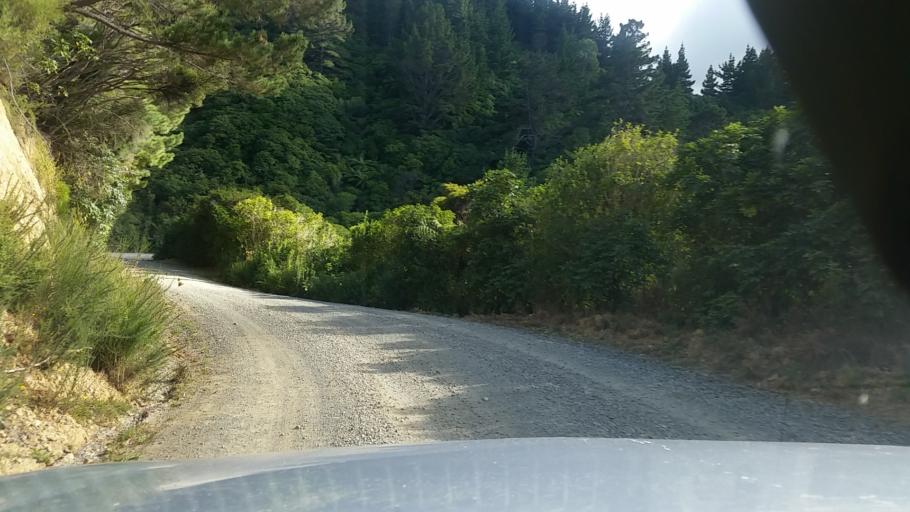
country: NZ
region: Marlborough
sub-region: Marlborough District
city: Picton
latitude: -41.2880
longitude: 174.1307
